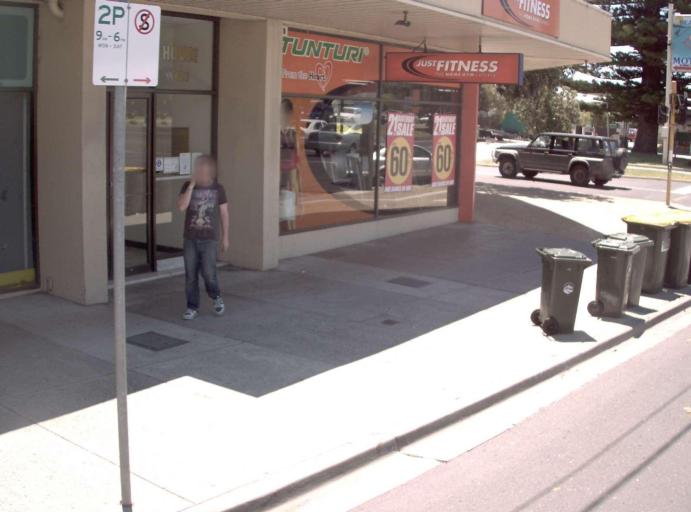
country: AU
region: Victoria
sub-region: Frankston
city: Frankston
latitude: -38.1404
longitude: 145.1222
